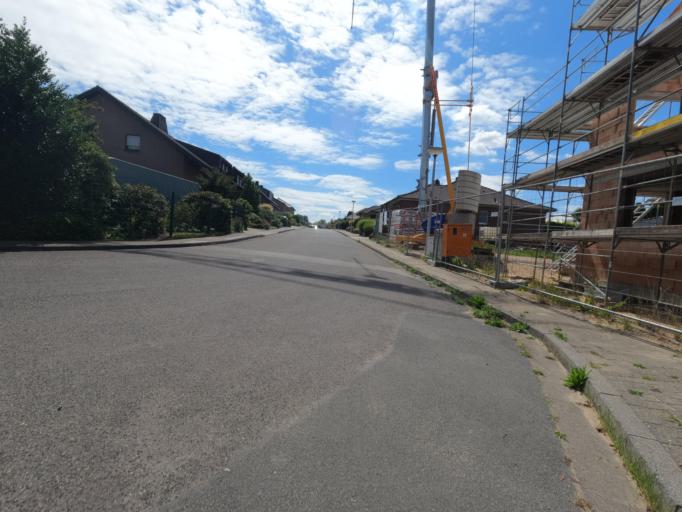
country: DE
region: North Rhine-Westphalia
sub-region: Regierungsbezirk Koln
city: Heinsberg
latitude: 51.0504
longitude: 6.1314
